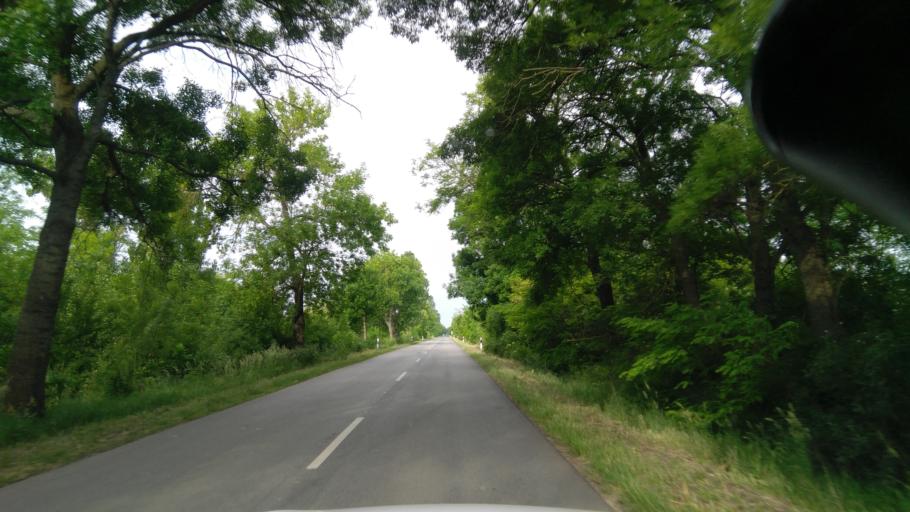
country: HU
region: Bekes
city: Ketegyhaza
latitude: 46.5358
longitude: 21.1305
